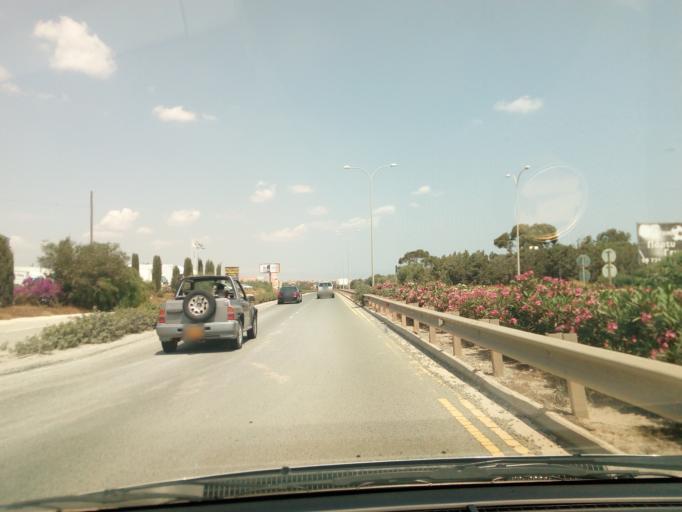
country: CY
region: Ammochostos
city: Ayia Napa
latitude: 35.0089
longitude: 33.9945
